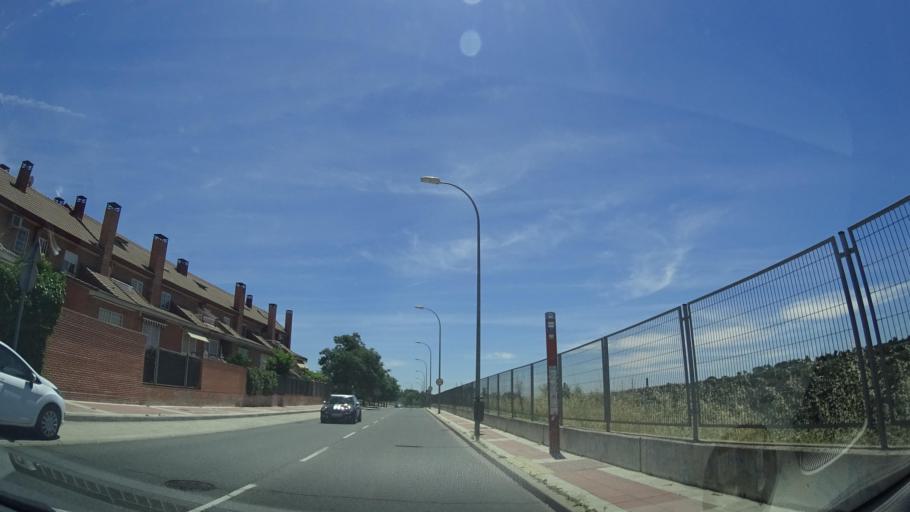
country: ES
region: Madrid
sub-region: Provincia de Madrid
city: Collado-Villalba
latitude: 40.6220
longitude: -3.9966
